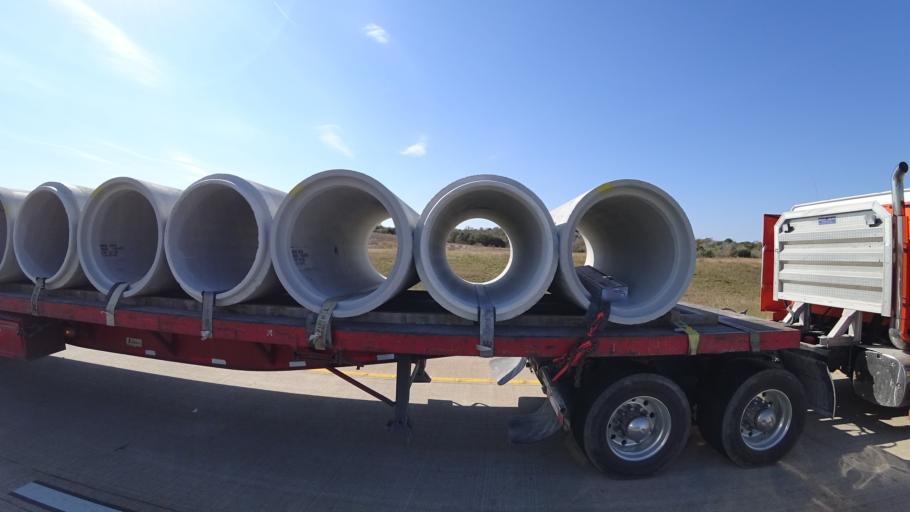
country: US
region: Texas
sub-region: Travis County
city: Manor
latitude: 30.3152
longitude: -97.5731
